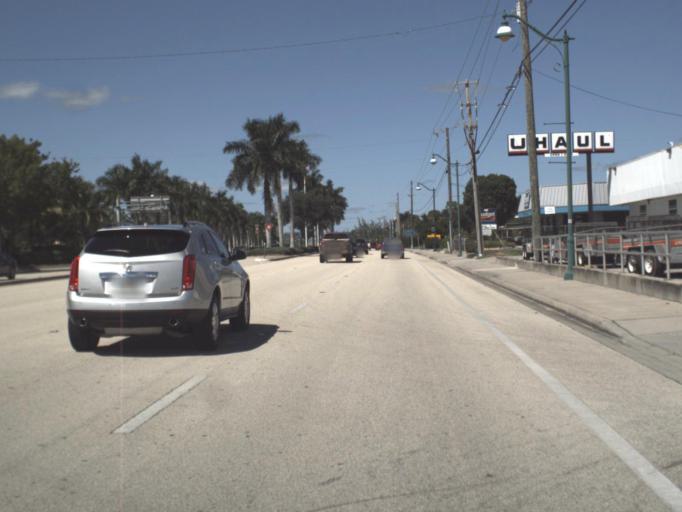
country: US
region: Florida
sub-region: Collier County
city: Naples
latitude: 26.1361
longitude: -81.7793
